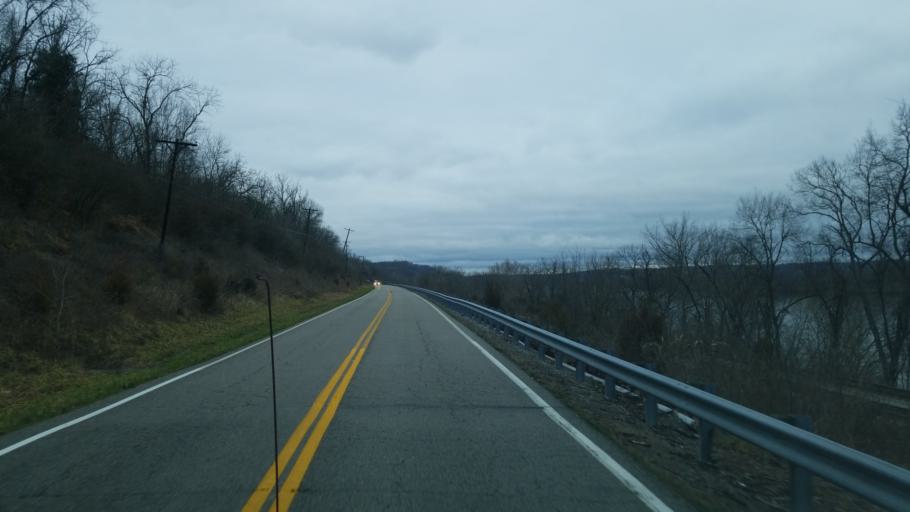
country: US
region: Ohio
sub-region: Clermont County
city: New Richmond
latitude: 38.9536
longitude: -84.2945
